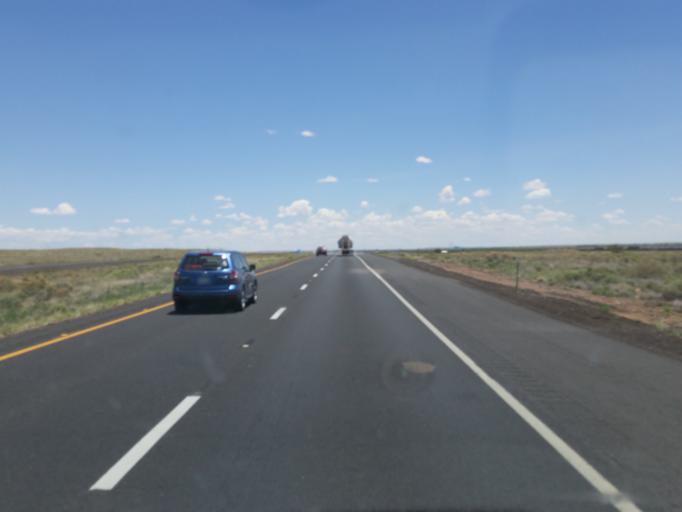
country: US
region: Arizona
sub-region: Navajo County
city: Joseph City
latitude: 34.9717
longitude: -110.4848
